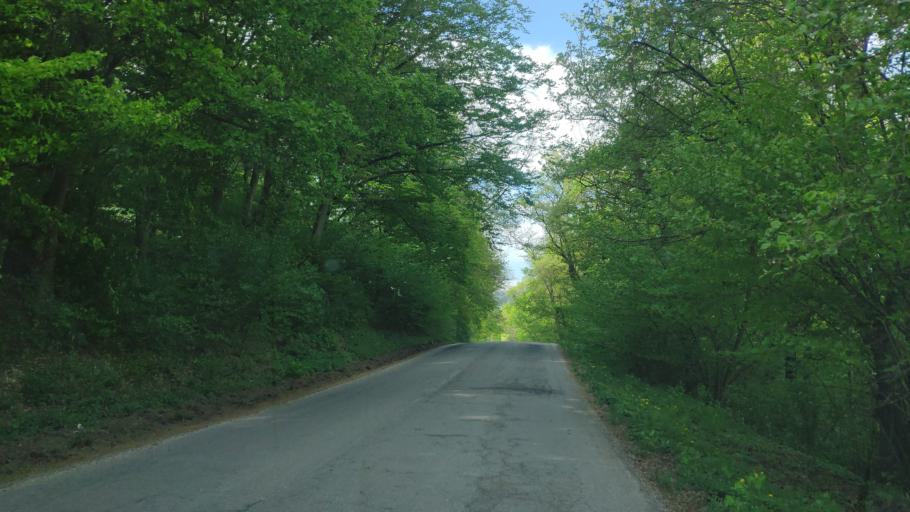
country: SK
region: Kosicky
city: Moldava nad Bodvou
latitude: 48.5866
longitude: 20.9126
